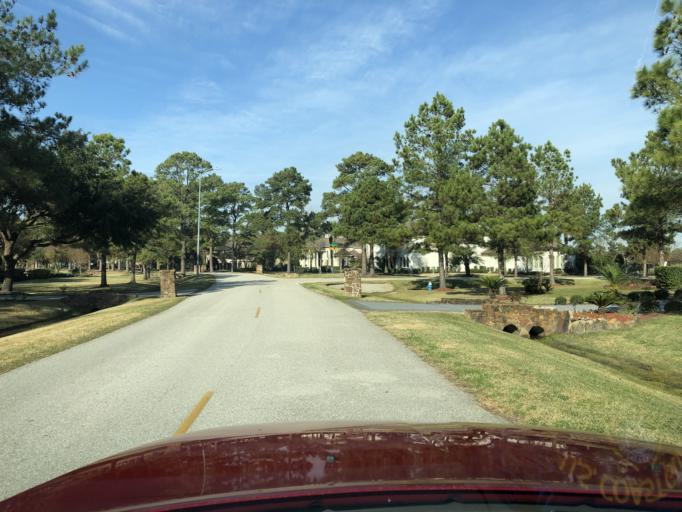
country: US
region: Texas
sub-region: Harris County
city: Tomball
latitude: 30.0424
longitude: -95.5585
